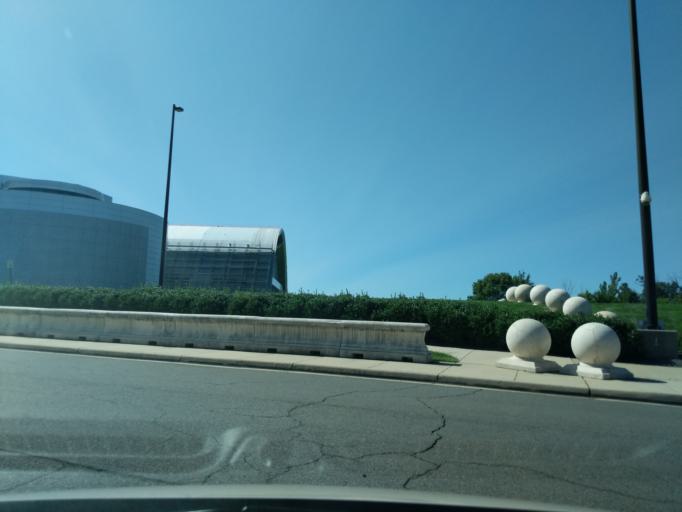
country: US
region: Virginia
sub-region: Fairfax County
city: Chantilly
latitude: 38.9124
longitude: -77.4420
